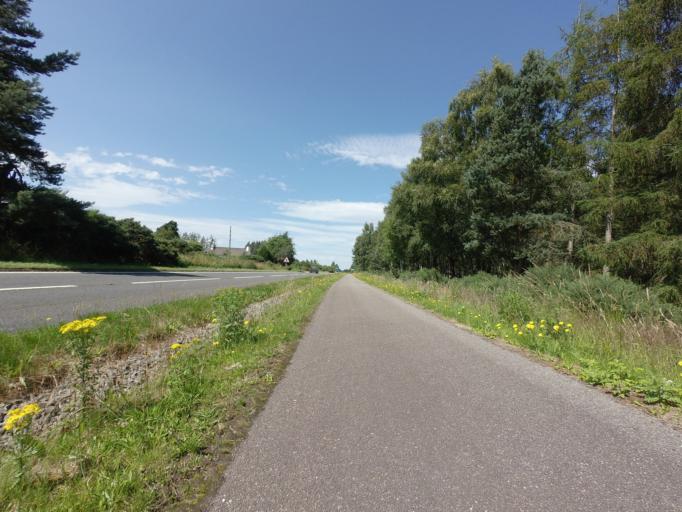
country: GB
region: Scotland
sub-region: Highland
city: Conon Bridge
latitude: 57.5405
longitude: -4.3733
